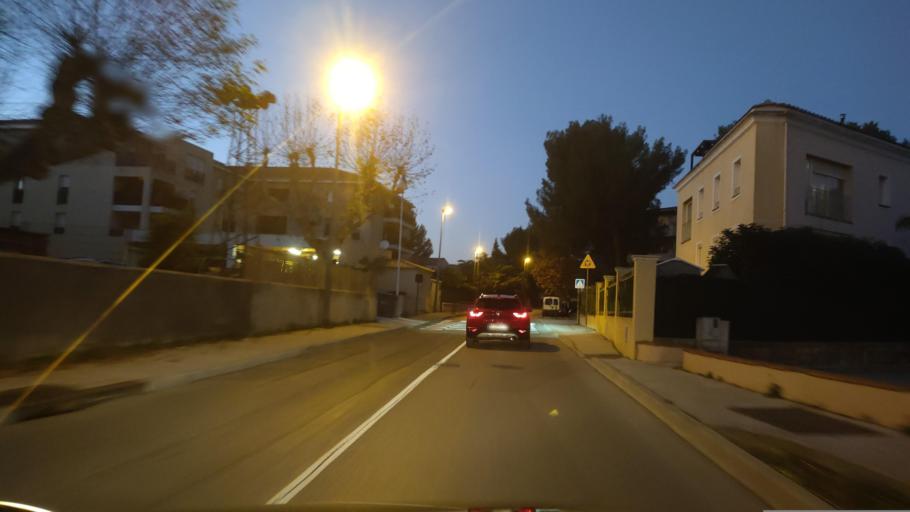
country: FR
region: Provence-Alpes-Cote d'Azur
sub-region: Departement du Var
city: Sanary-sur-Mer
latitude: 43.1226
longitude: 5.8038
